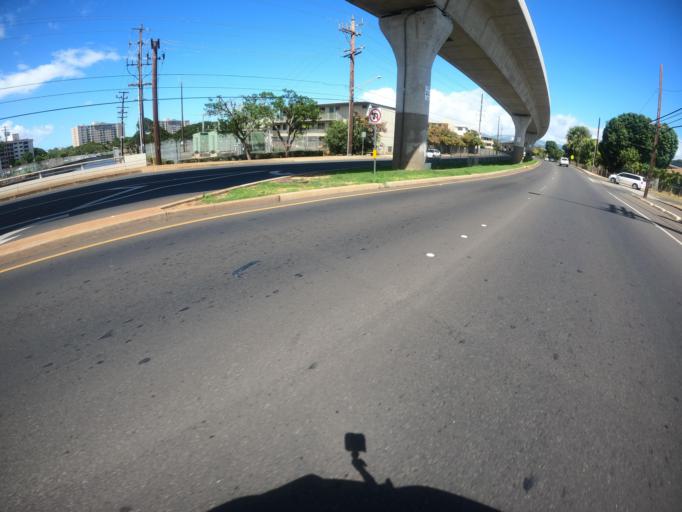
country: US
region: Hawaii
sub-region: Honolulu County
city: Waipahu
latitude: 21.3847
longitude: -158.0009
